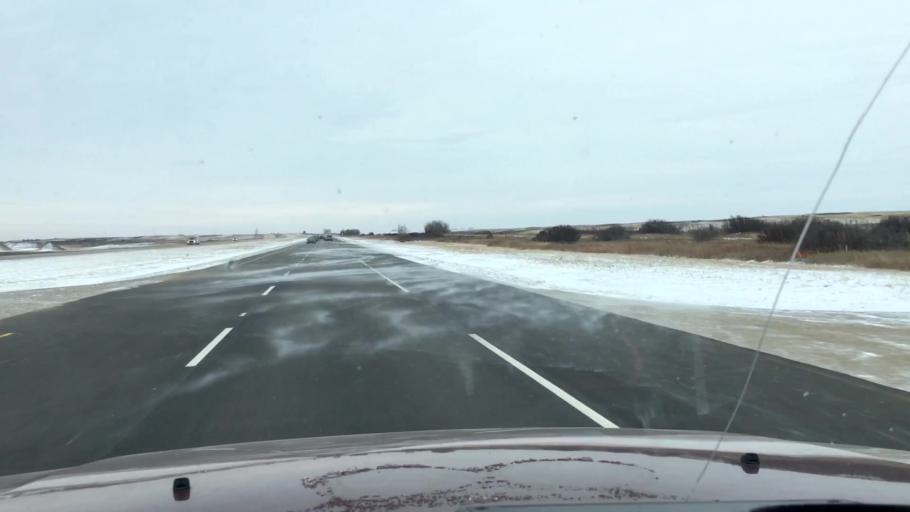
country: CA
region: Saskatchewan
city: Moose Jaw
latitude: 50.8921
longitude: -105.6269
